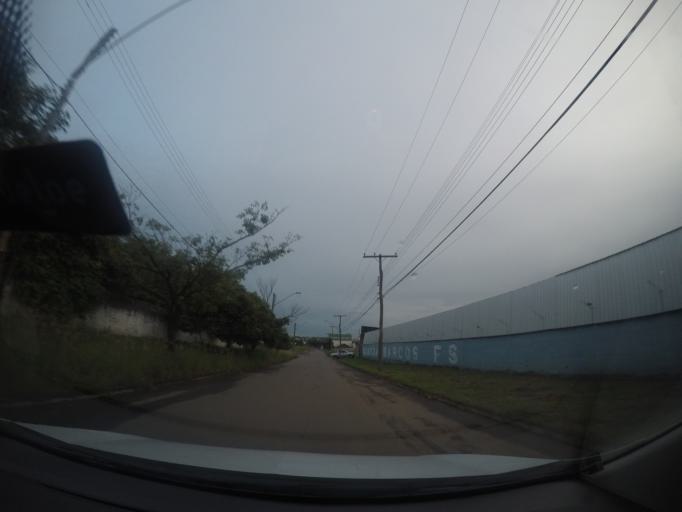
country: BR
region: Goias
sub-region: Goiania
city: Goiania
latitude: -16.6415
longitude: -49.2432
